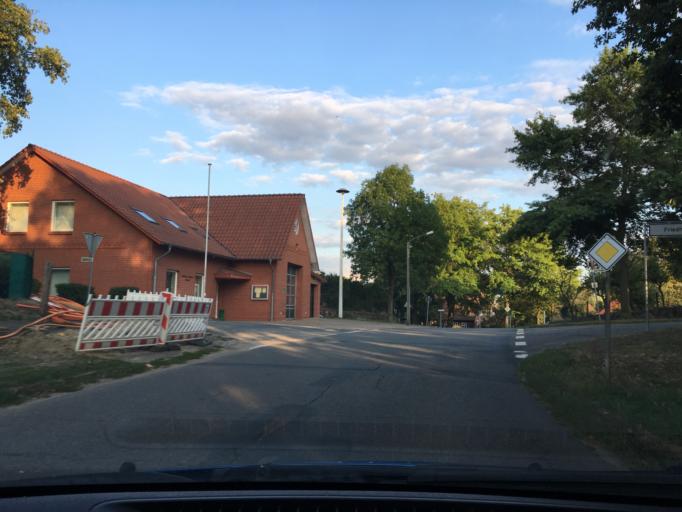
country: DE
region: Lower Saxony
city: Bleckede
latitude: 53.2650
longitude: 10.7056
